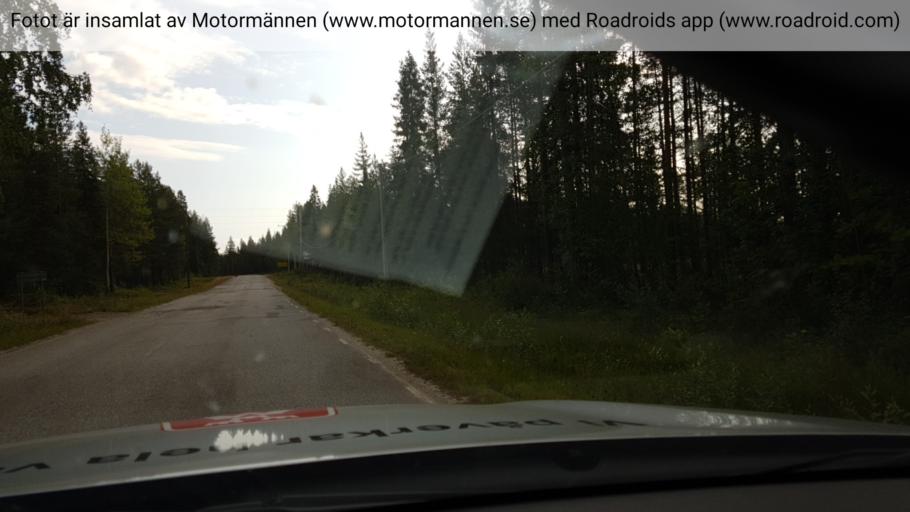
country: SE
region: Vaesterbotten
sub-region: Skelleftea Kommun
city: Storvik
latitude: 65.5036
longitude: 20.4936
